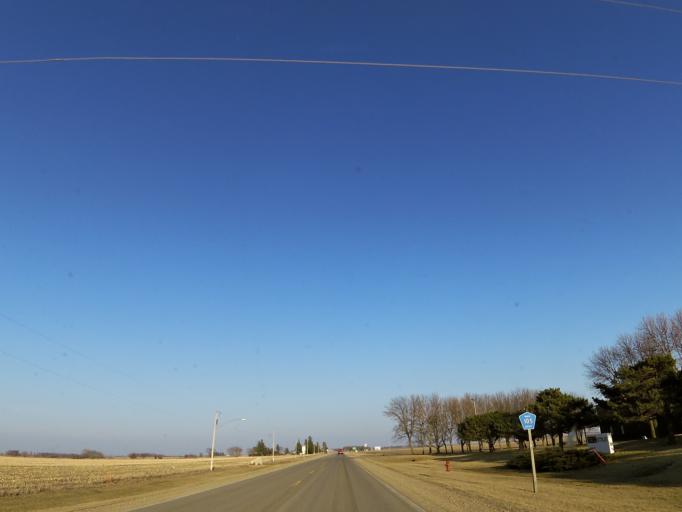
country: US
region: Iowa
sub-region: Worth County
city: Northwood
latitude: 43.4440
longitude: -93.1978
